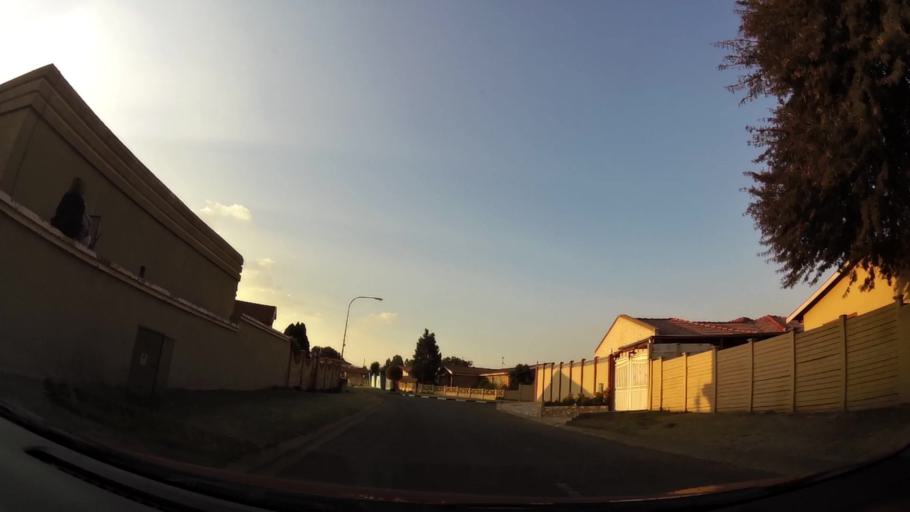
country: ZA
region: Gauteng
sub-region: City of Johannesburg Metropolitan Municipality
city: Soweto
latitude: -26.2824
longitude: 27.9028
